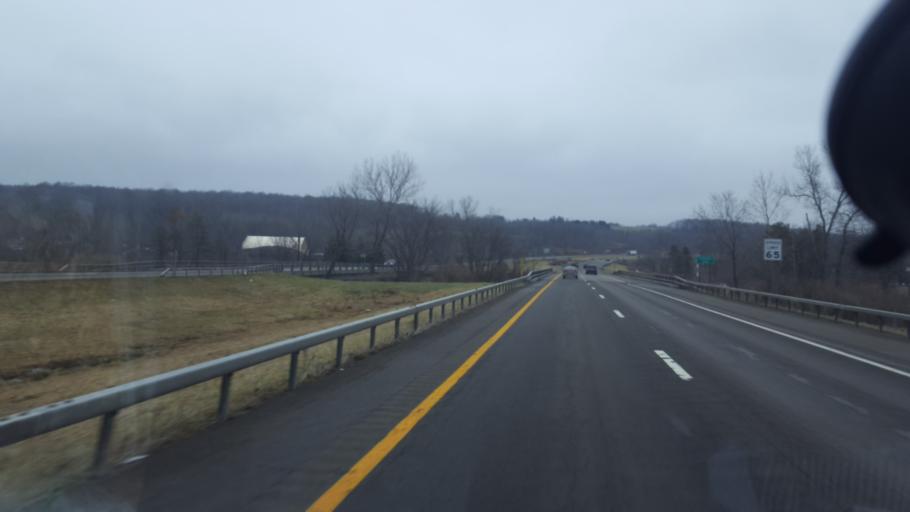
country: US
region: New York
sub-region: Chautauqua County
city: Falconer
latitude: 42.1337
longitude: -79.1840
